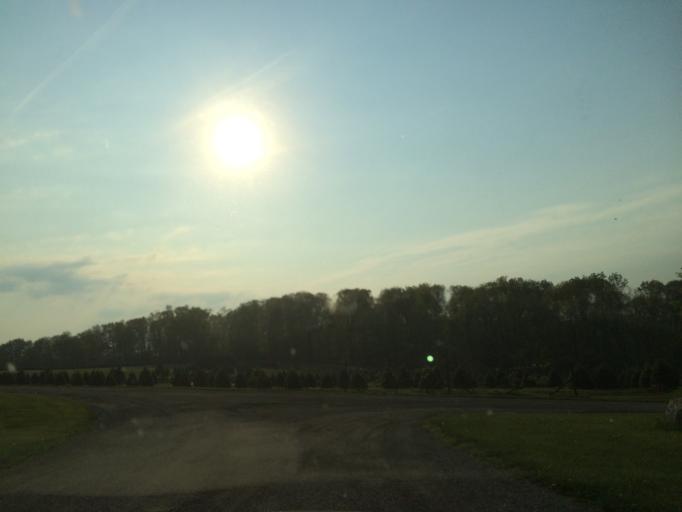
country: US
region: Maryland
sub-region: Carroll County
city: Sykesville
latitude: 39.4046
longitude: -77.0350
